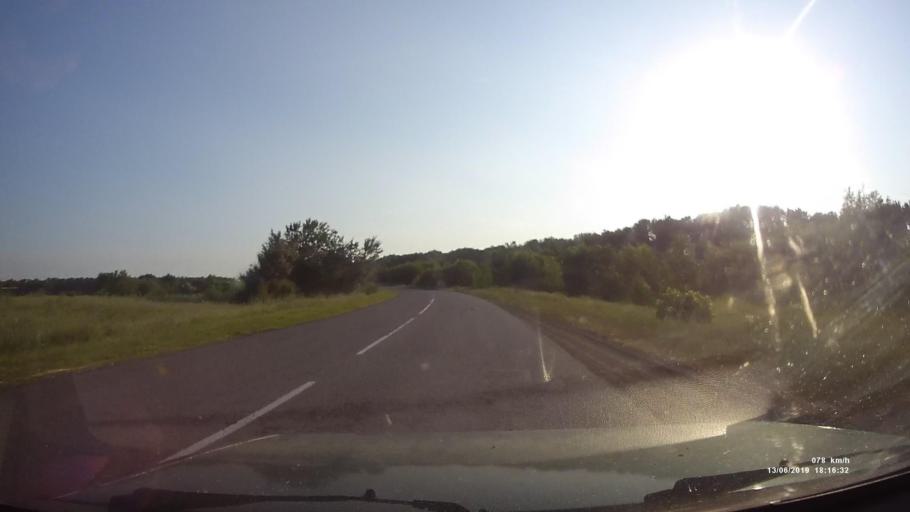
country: RU
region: Rostov
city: Kazanskaya
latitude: 49.9268
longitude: 41.3384
